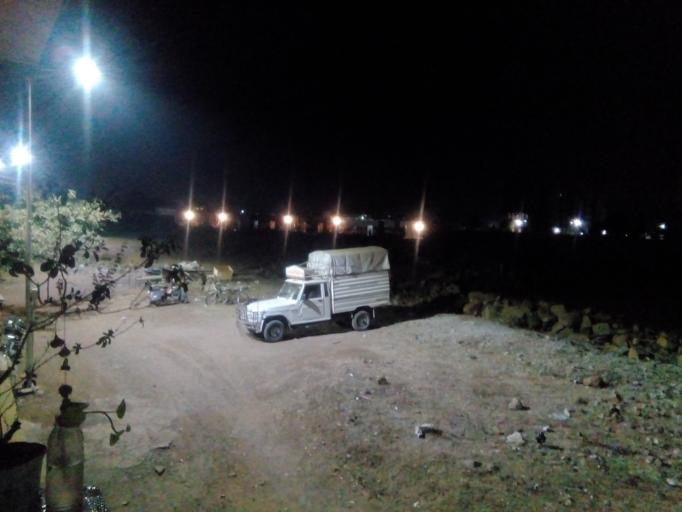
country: IN
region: Maharashtra
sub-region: Pune Division
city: Lohogaon
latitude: 18.5604
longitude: 73.9540
